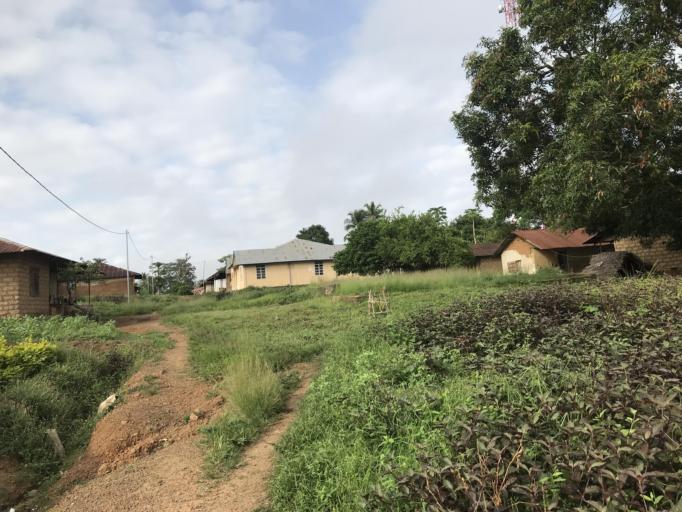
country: SL
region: Eastern Province
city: Pendembu
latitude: 8.1011
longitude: -10.6954
